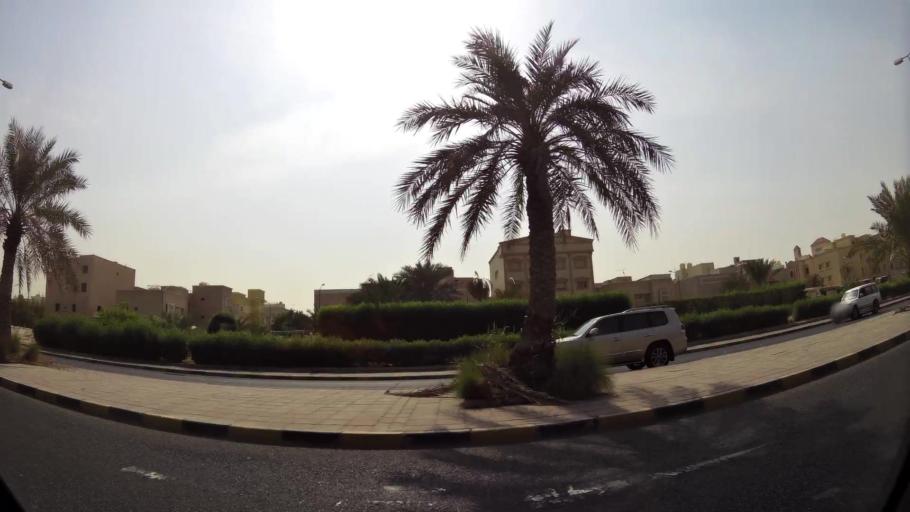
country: KW
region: Al Asimah
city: Ar Rabiyah
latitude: 29.3029
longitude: 47.8678
